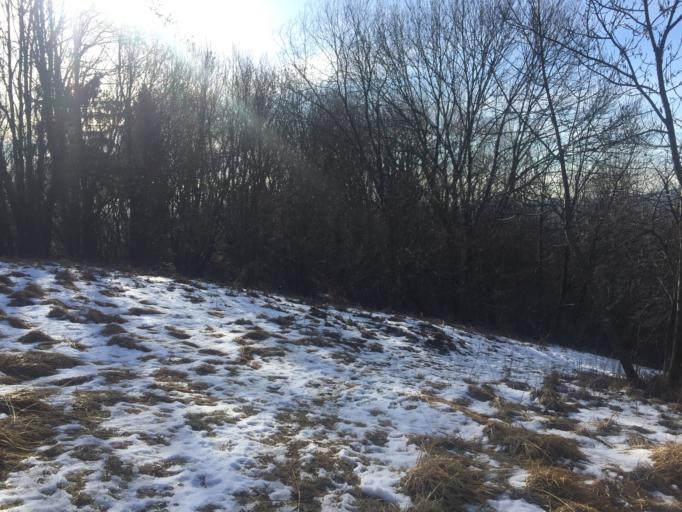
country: IT
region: Friuli Venezia Giulia
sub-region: Provincia di Udine
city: Clodig
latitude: 46.1694
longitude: 13.5843
